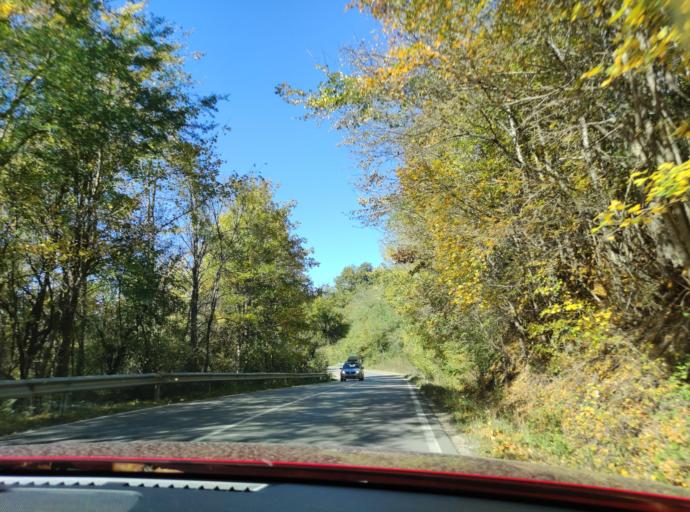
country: BG
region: Montana
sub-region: Obshtina Chiprovtsi
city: Chiprovtsi
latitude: 43.4078
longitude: 23.0519
